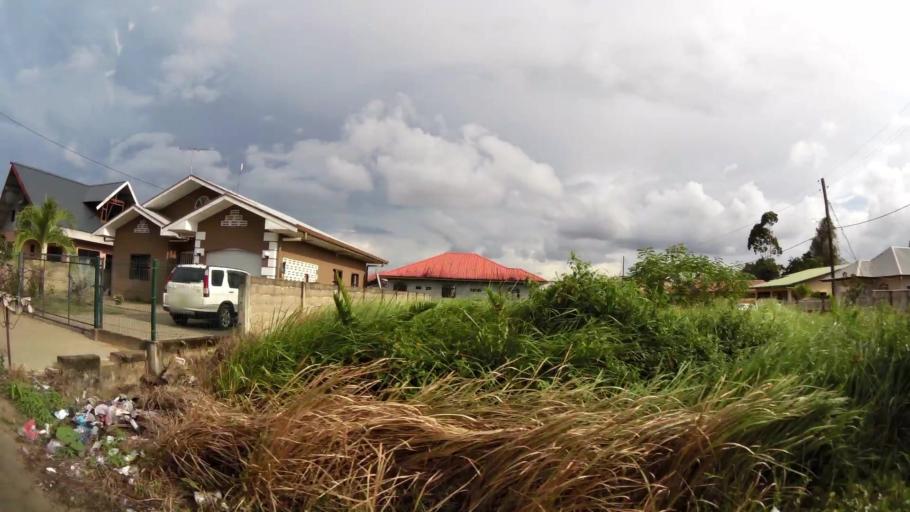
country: SR
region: Paramaribo
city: Paramaribo
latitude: 5.8504
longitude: -55.1779
